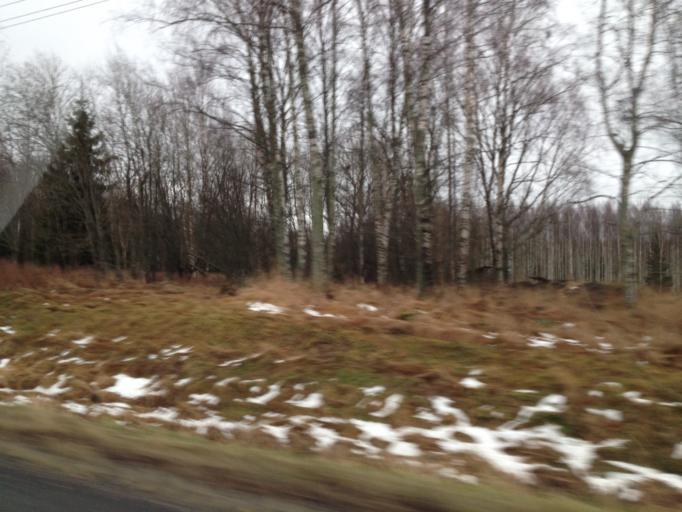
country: FI
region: Uusimaa
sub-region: Raaseporin
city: Ekenaes
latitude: 59.9580
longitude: 23.3695
